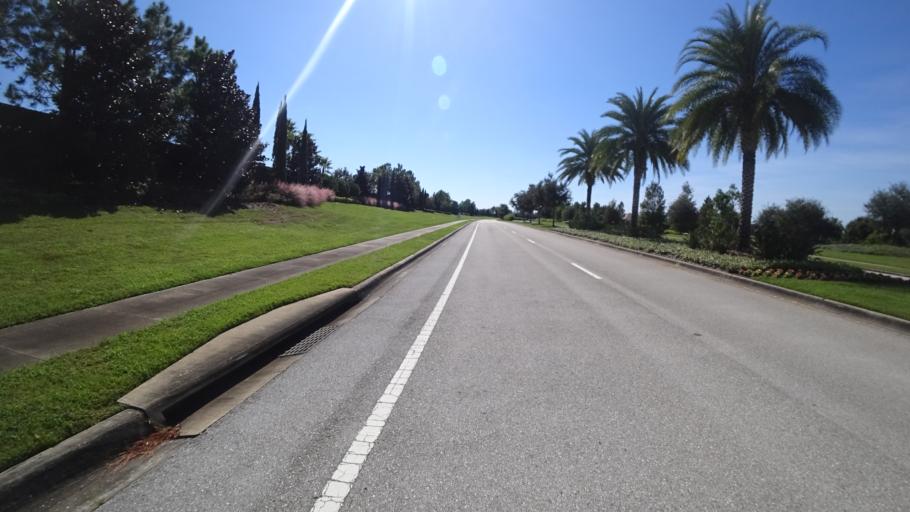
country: US
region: Florida
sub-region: Sarasota County
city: The Meadows
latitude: 27.4001
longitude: -82.3833
